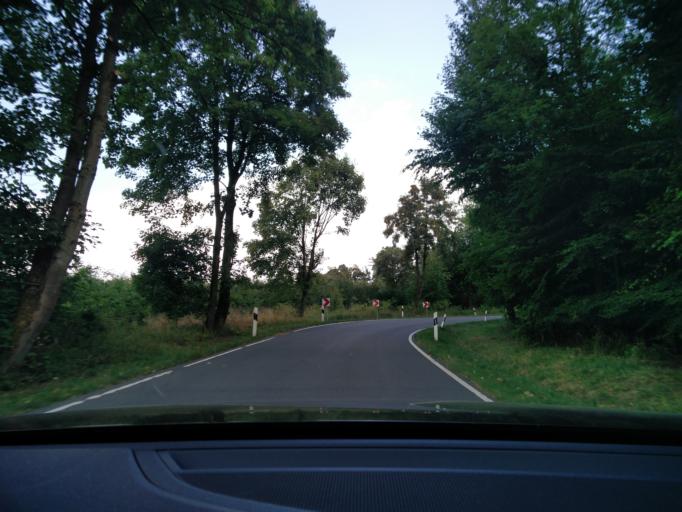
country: DE
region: North Rhine-Westphalia
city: Lichtenau
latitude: 51.6868
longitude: 8.9036
